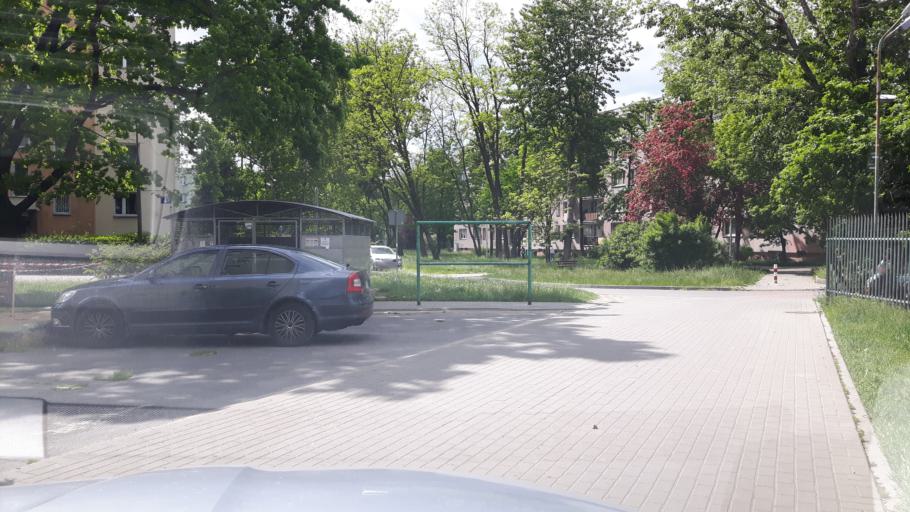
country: PL
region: Masovian Voivodeship
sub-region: Warszawa
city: Targowek
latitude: 52.2951
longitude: 21.0252
